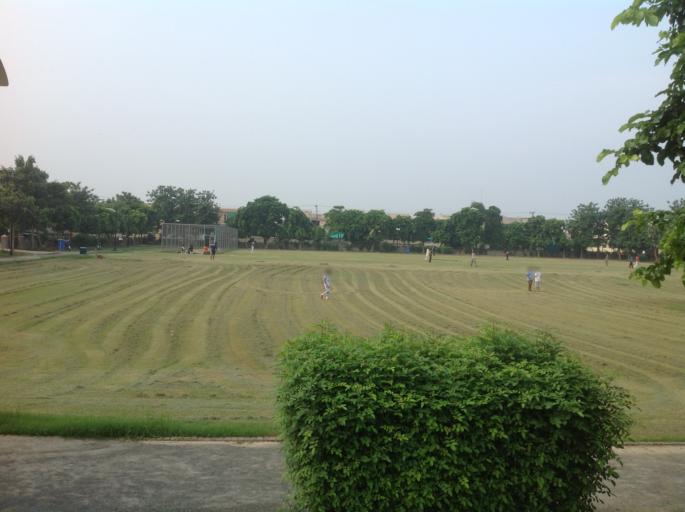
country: PK
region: Punjab
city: Kahna
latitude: 31.4546
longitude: 74.3865
